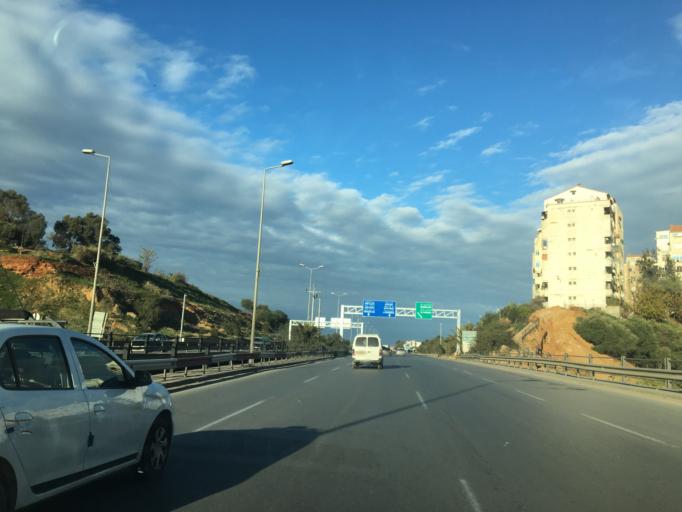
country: DZ
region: Alger
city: Bab Ezzouar
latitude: 36.7304
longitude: 3.1181
